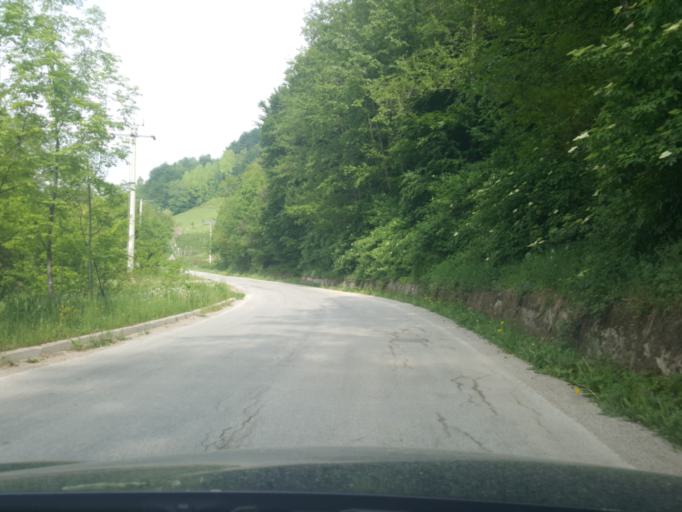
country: RS
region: Central Serbia
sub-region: Zlatiborski Okrug
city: Bajina Basta
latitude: 44.0684
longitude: 19.6470
